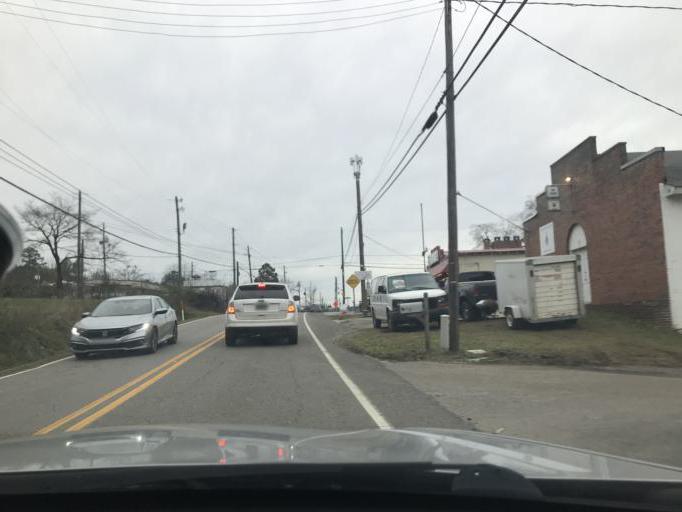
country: US
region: Alabama
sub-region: Jefferson County
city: Cahaba Heights
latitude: 33.4541
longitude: -86.7255
